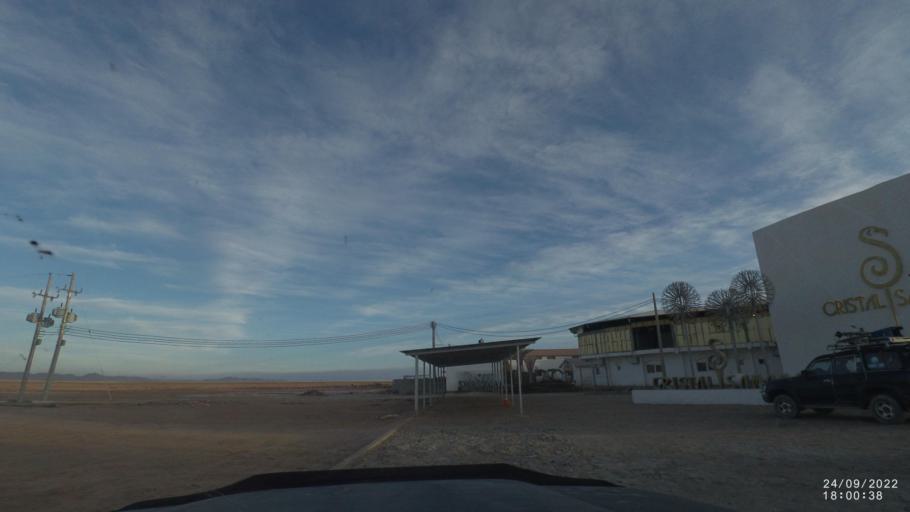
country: BO
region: Potosi
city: Colchani
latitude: -20.3117
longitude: -66.9714
